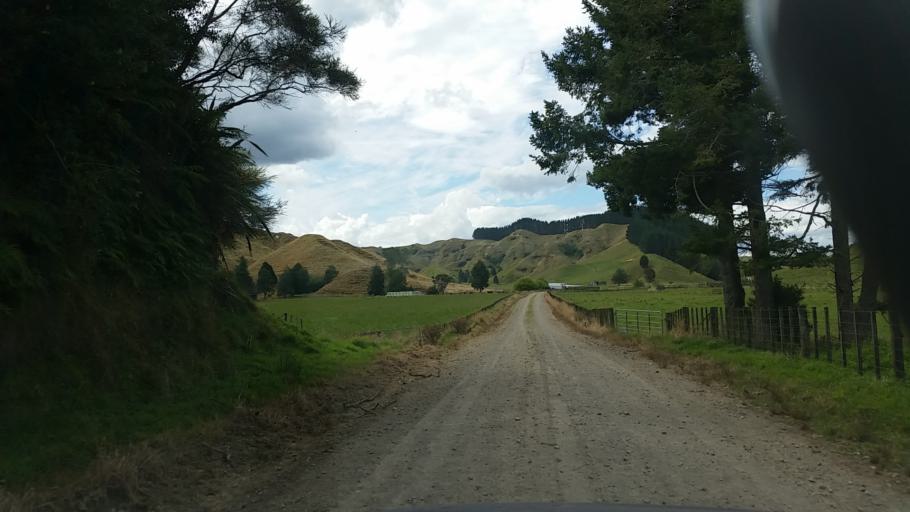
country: NZ
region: Taranaki
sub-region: South Taranaki District
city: Eltham
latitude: -39.2856
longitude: 174.4961
